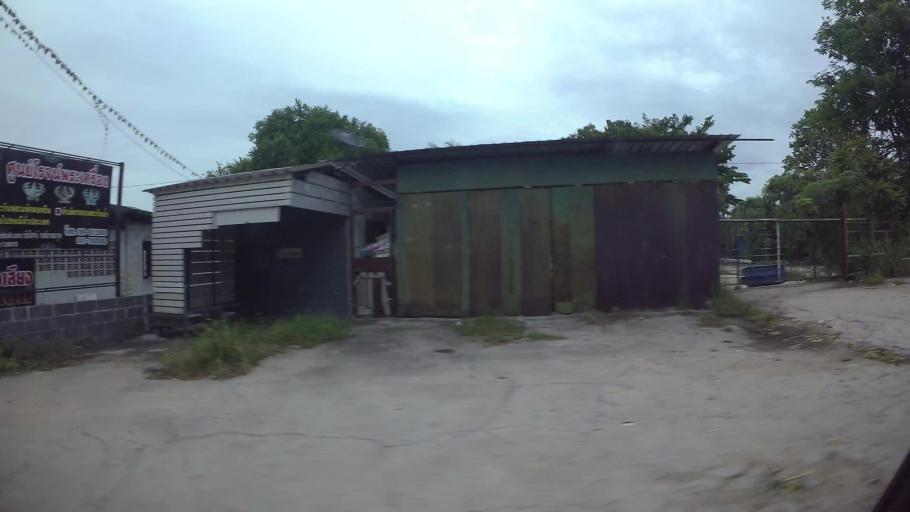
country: TH
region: Chon Buri
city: Si Racha
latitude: 13.1441
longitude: 100.9446
